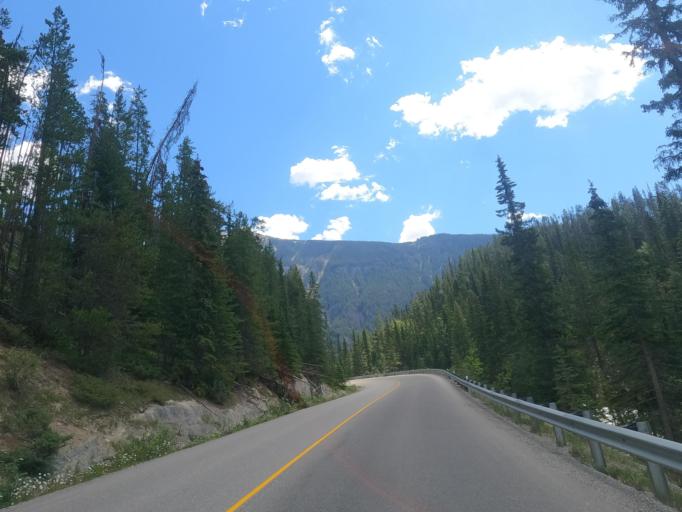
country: CA
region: Alberta
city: Lake Louise
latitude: 51.3811
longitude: -116.5244
